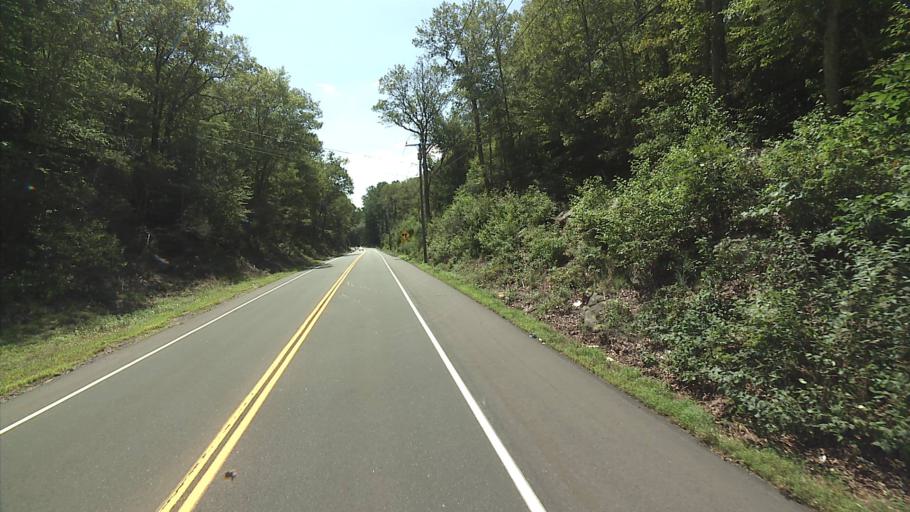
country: US
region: Connecticut
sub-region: New London County
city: Niantic
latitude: 41.3451
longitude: -72.2696
